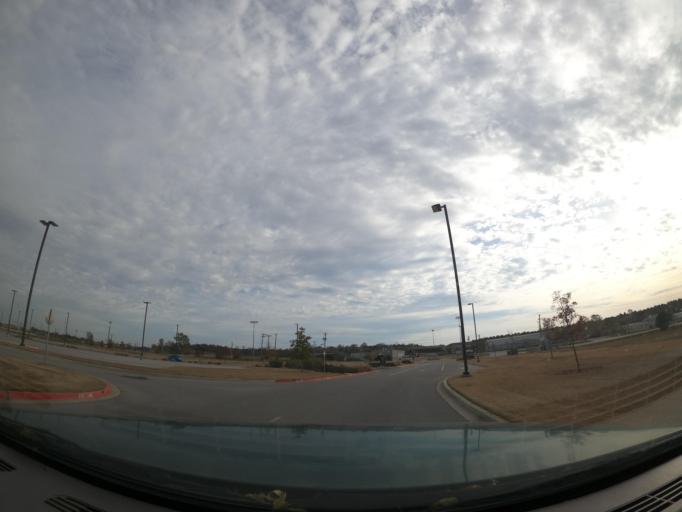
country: US
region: Oklahoma
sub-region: Tulsa County
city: Turley
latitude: 36.2067
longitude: -96.0061
